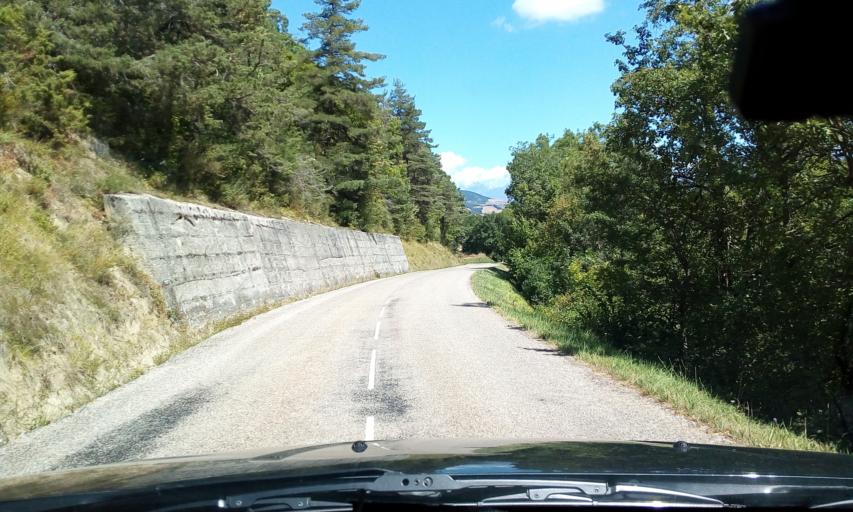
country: FR
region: Rhone-Alpes
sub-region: Departement de l'Isere
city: Mens
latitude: 44.7790
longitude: 5.6716
